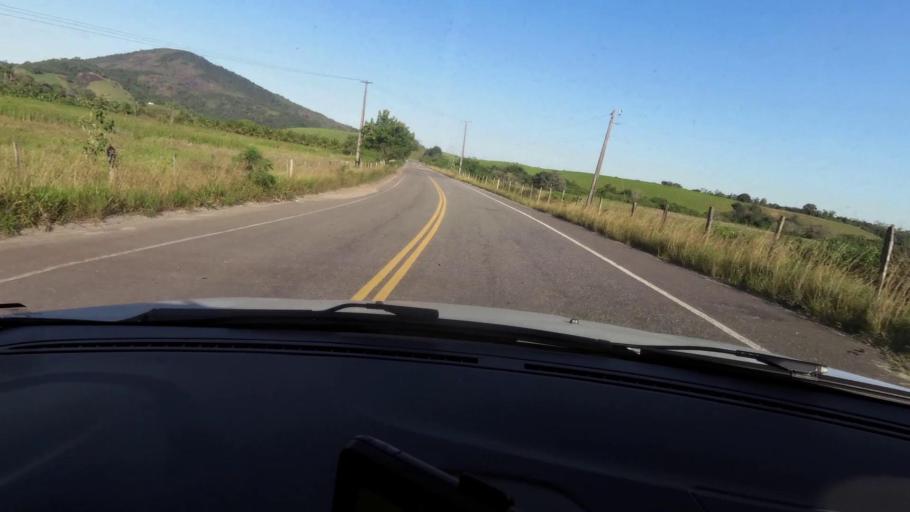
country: BR
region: Espirito Santo
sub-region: Piuma
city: Piuma
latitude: -20.7360
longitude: -40.6505
